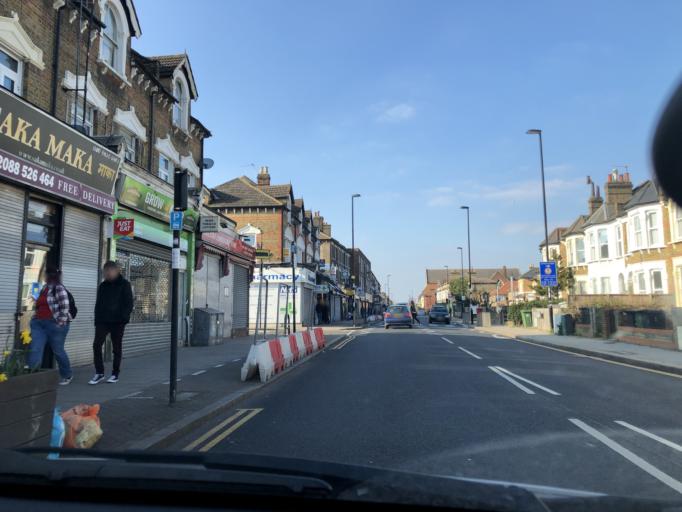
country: GB
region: England
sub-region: Greater London
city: Catford
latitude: 51.4503
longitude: -0.0057
